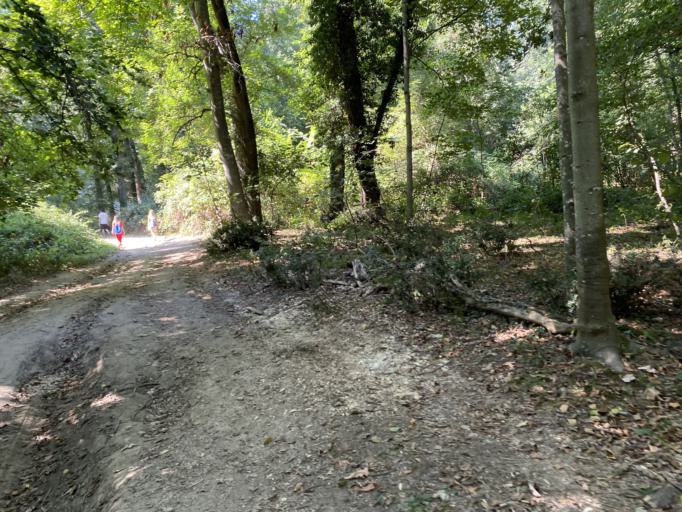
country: TR
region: Kirklareli
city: Igneada
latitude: 41.8211
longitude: 27.9647
